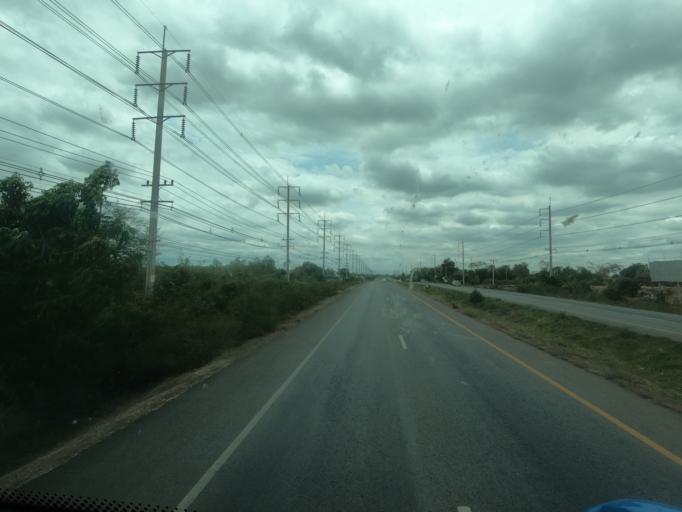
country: TH
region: Nakhon Ratchasima
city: Chok Chai
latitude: 14.7367
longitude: 102.1088
